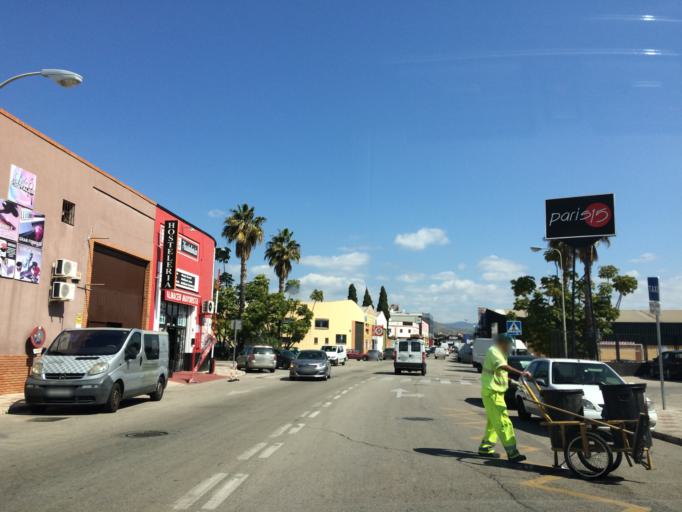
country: ES
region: Andalusia
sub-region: Provincia de Malaga
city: Malaga
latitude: 36.7049
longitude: -4.4765
